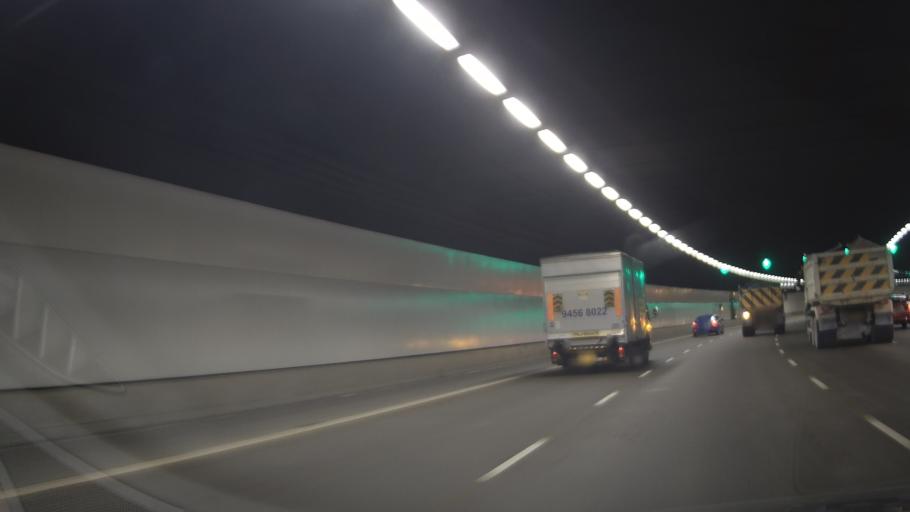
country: SG
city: Singapore
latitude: 1.2846
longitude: 103.8672
